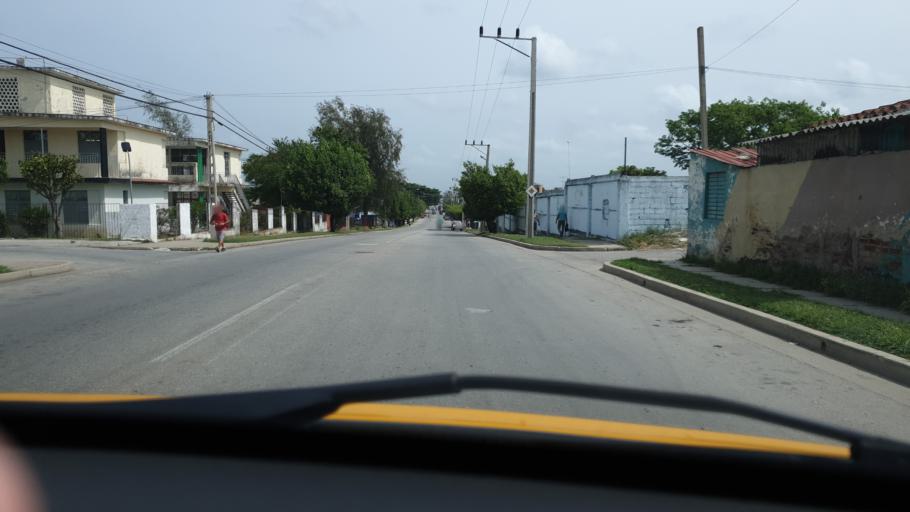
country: CU
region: Villa Clara
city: Santa Clara
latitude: 22.3906
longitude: -79.9603
